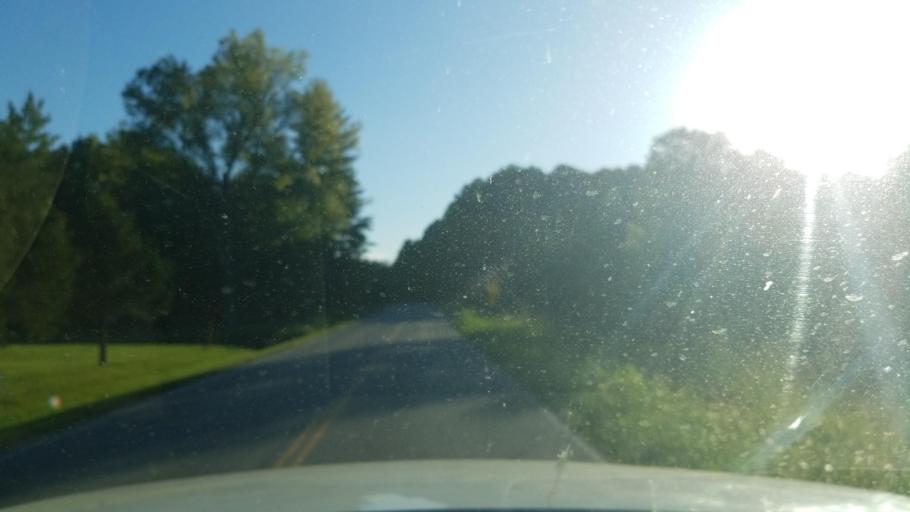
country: US
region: Illinois
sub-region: Hardin County
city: Rosiclare
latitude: 37.5677
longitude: -88.4037
